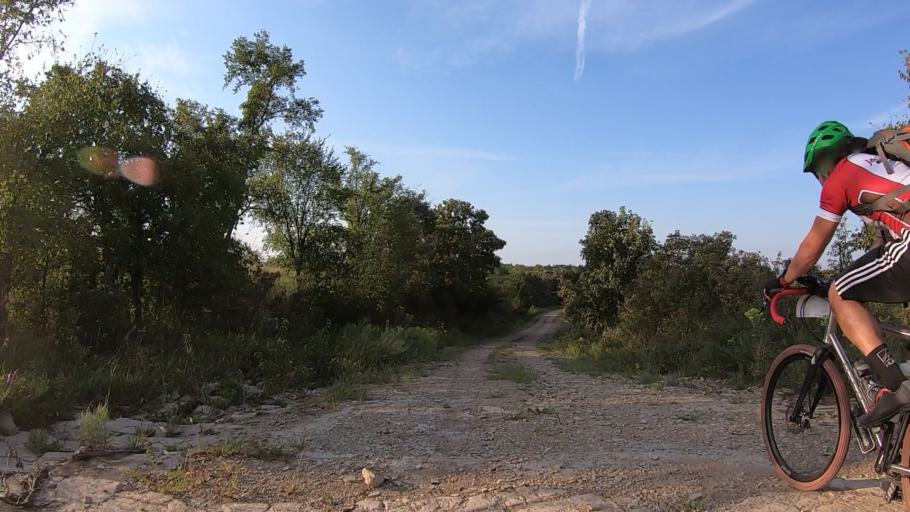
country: US
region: Kansas
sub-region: Marshall County
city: Blue Rapids
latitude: 39.7507
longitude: -96.7507
